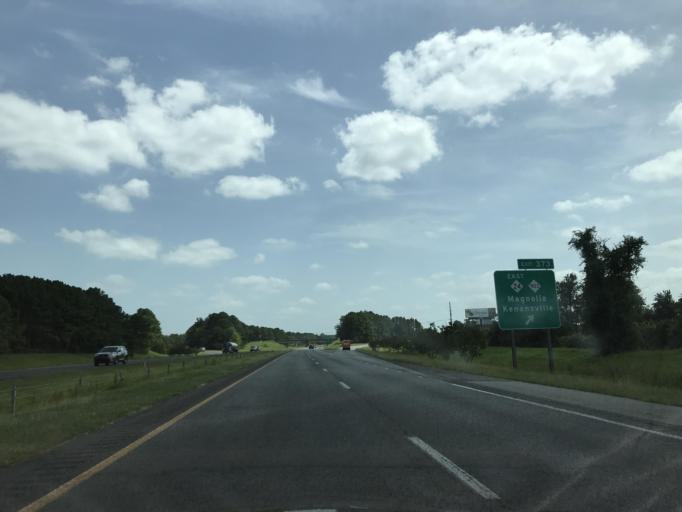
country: US
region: North Carolina
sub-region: Duplin County
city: Kenansville
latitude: 34.9216
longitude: -78.0285
